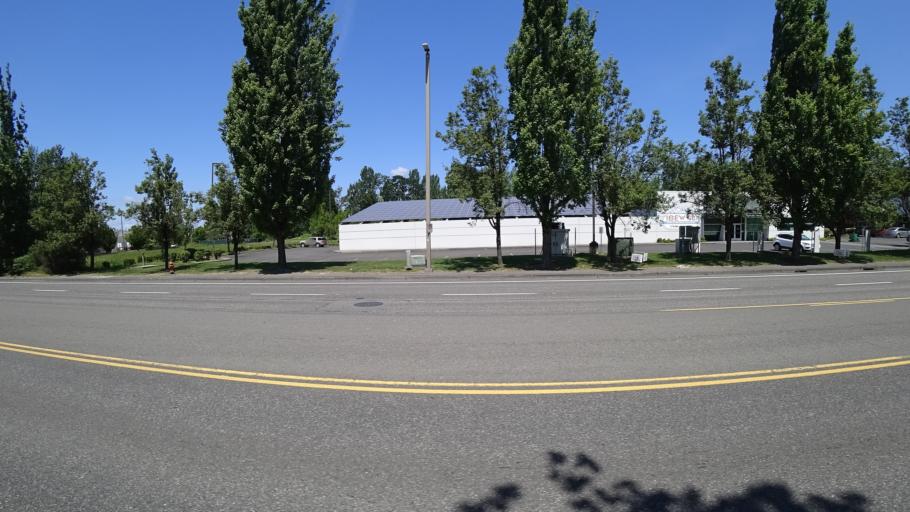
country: US
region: Oregon
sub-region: Multnomah County
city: Fairview
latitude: 45.5574
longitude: -122.4993
